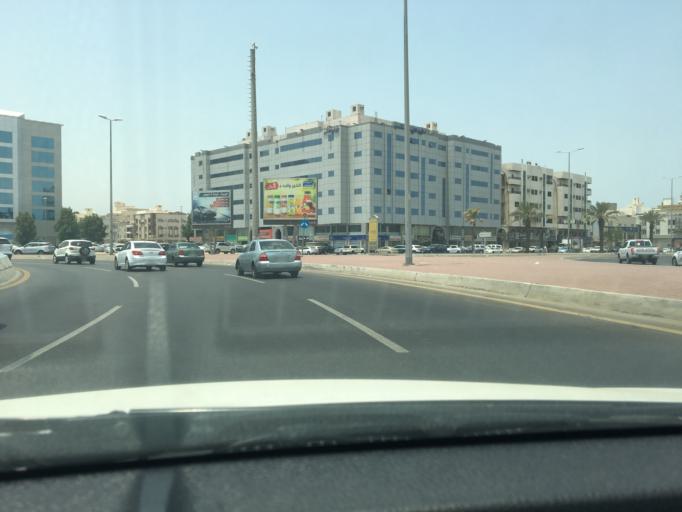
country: SA
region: Makkah
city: Jeddah
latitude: 21.5848
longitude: 39.1766
